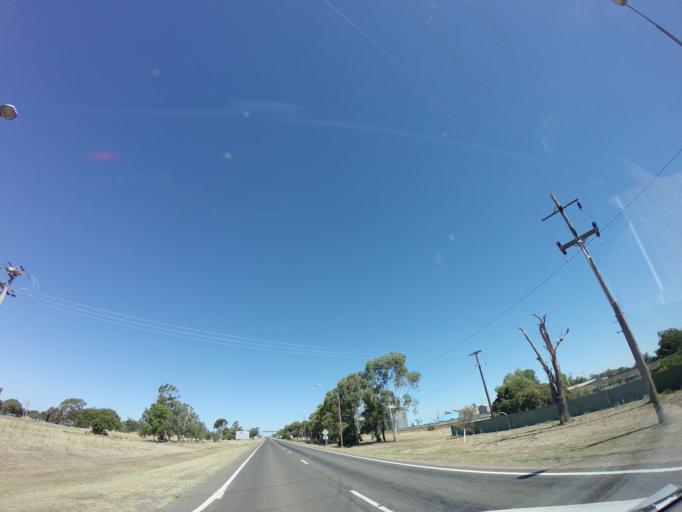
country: AU
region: New South Wales
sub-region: Bogan
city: Nyngan
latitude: -31.5671
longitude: 147.2063
